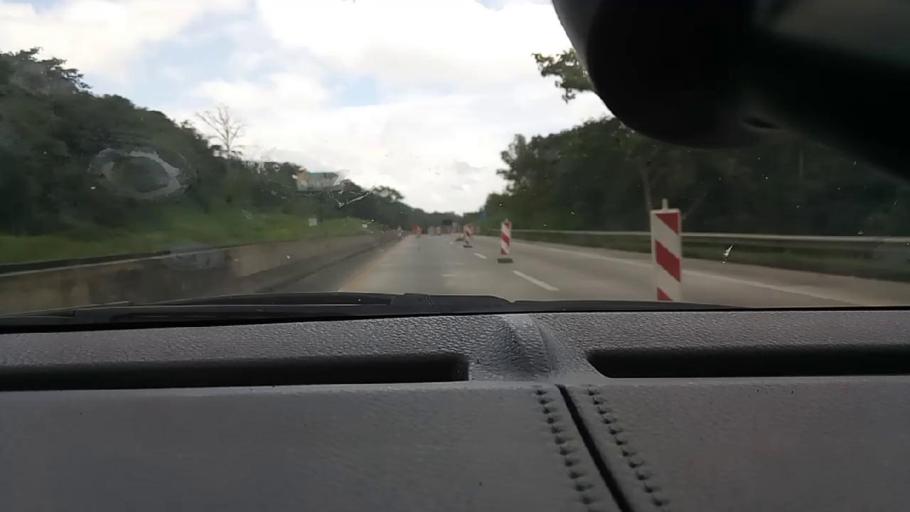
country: PA
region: Panama
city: Chilibre
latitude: 9.1603
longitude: -79.6381
